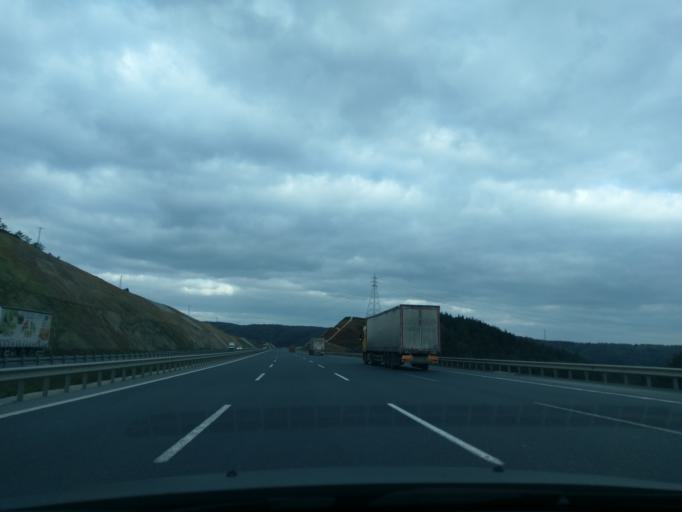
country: TR
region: Istanbul
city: Basaksehir
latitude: 41.1614
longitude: 28.8103
